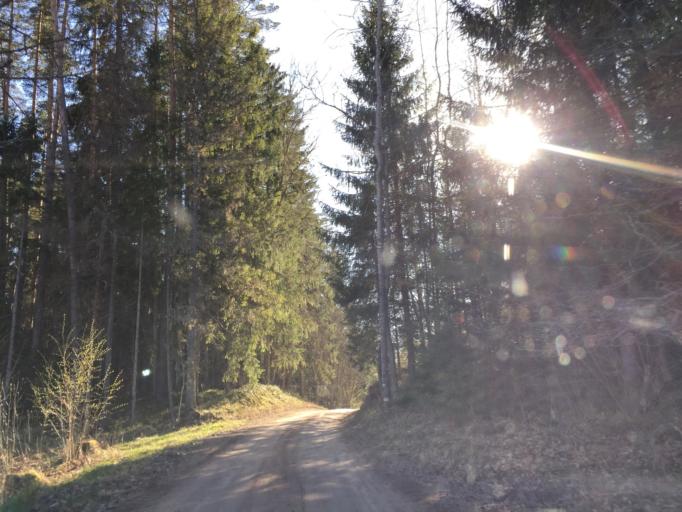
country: EE
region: Valgamaa
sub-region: Valga linn
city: Valga
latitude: 57.7735
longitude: 26.2243
